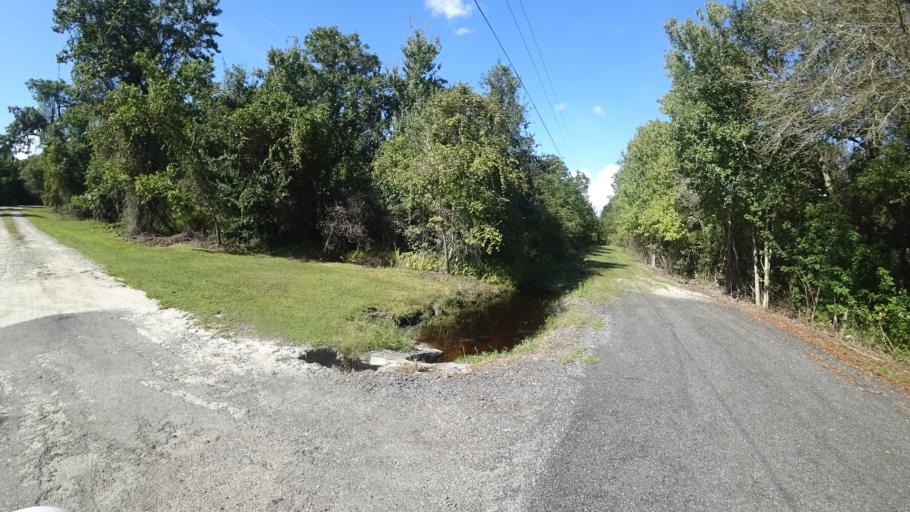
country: US
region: Florida
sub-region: Sarasota County
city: The Meadows
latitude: 27.4489
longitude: -82.2870
